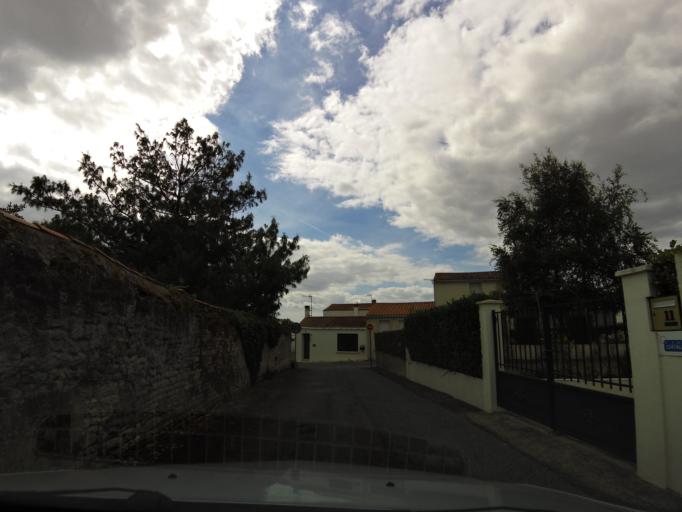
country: FR
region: Pays de la Loire
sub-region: Departement de la Vendee
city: Longeville-sur-Mer
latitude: 46.4244
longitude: -1.4914
